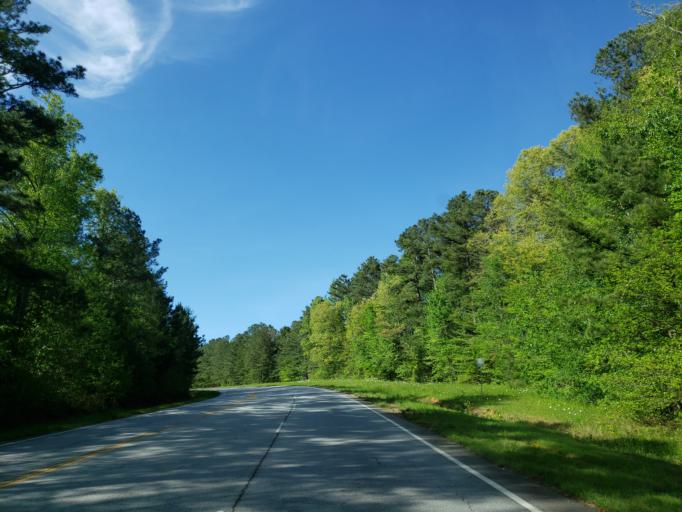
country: US
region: Georgia
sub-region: Haralson County
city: Tallapoosa
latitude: 33.7108
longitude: -85.2711
